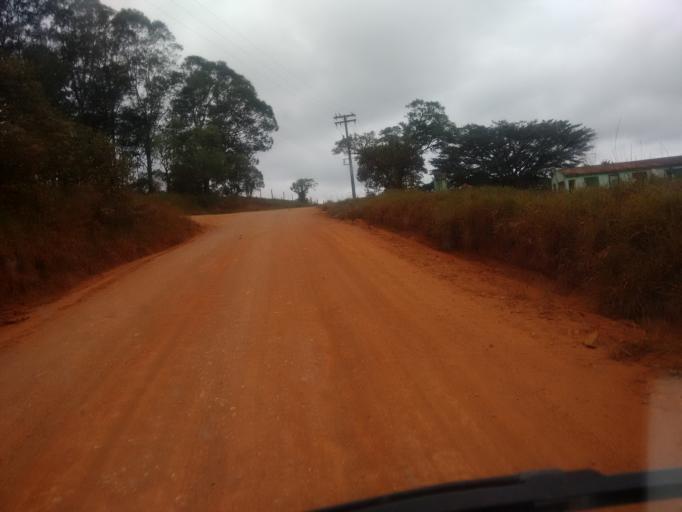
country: BR
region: Rio Grande do Sul
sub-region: Camaqua
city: Camaqua
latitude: -30.7879
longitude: -51.8326
